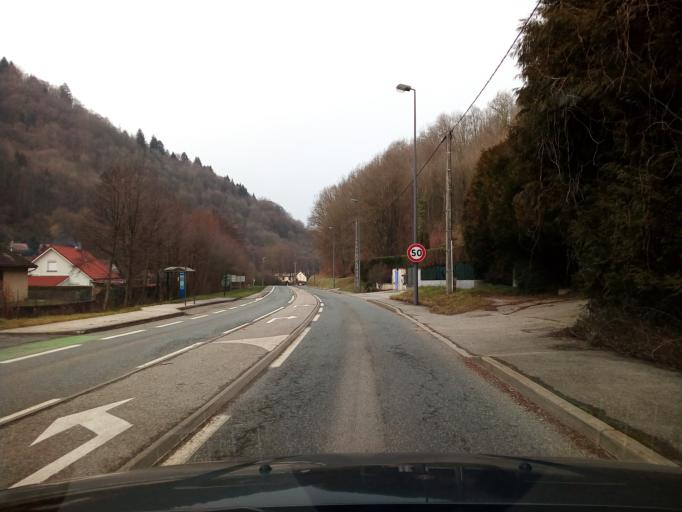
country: FR
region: Rhone-Alpes
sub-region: Departement de l'Isere
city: Herbeys
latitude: 45.1571
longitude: 5.8228
